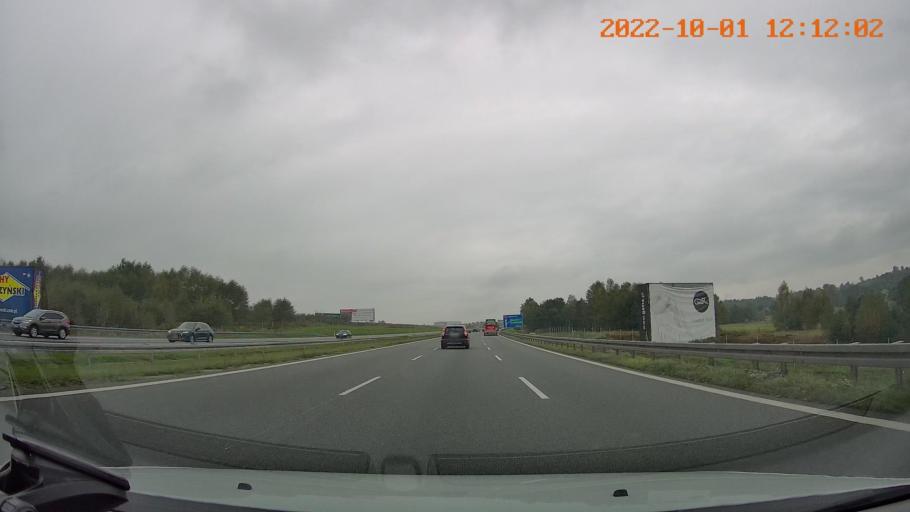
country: PL
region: Lesser Poland Voivodeship
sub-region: Powiat chrzanowski
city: Grojec
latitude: 50.0922
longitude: 19.5746
